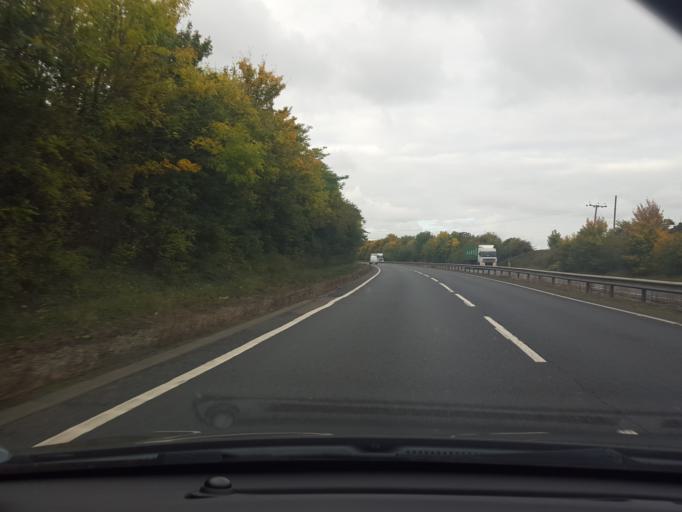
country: GB
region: England
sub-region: Suffolk
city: Stowmarket
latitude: 52.1924
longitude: 1.0145
